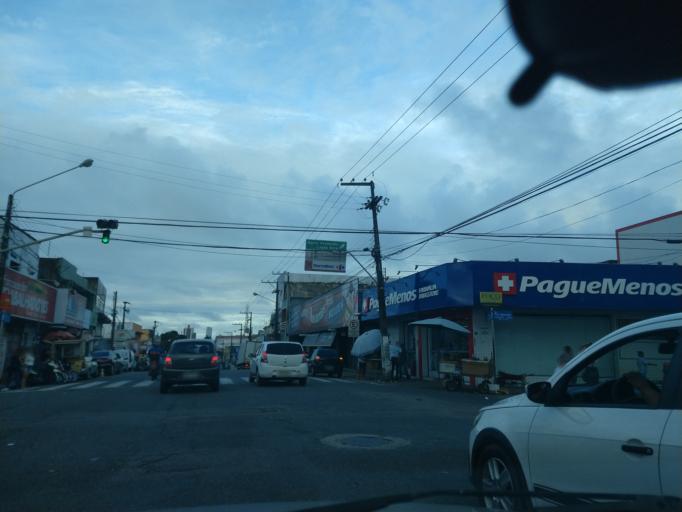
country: BR
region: Rio Grande do Norte
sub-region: Natal
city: Natal
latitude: -5.7960
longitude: -35.2165
